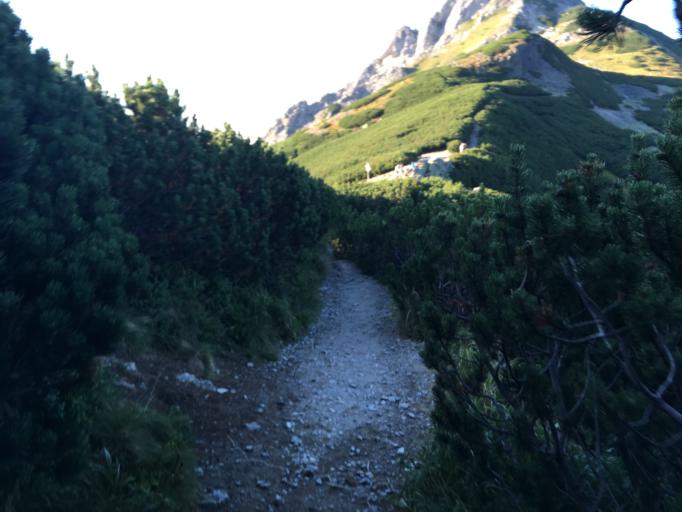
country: PL
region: Lesser Poland Voivodeship
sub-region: Powiat tatrzanski
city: Zakopane
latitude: 49.2458
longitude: 19.9323
